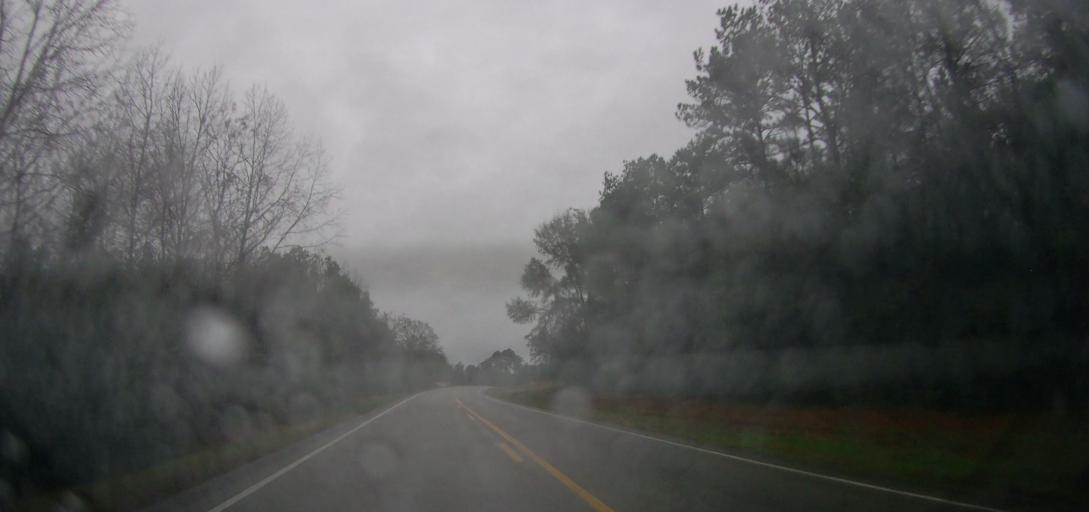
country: US
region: Alabama
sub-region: Autauga County
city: Pine Level
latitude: 32.5483
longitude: -86.6491
